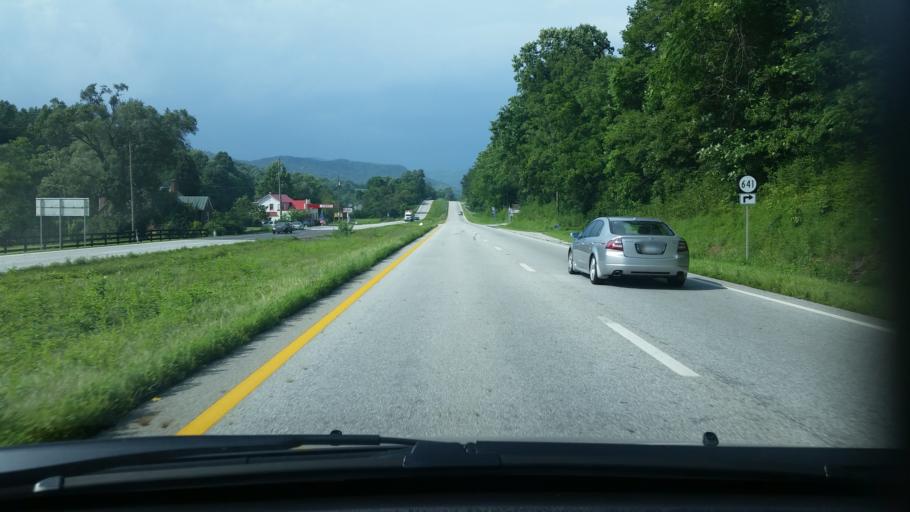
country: US
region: Virginia
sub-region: Nelson County
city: Lovingston
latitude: 37.7795
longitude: -78.8684
